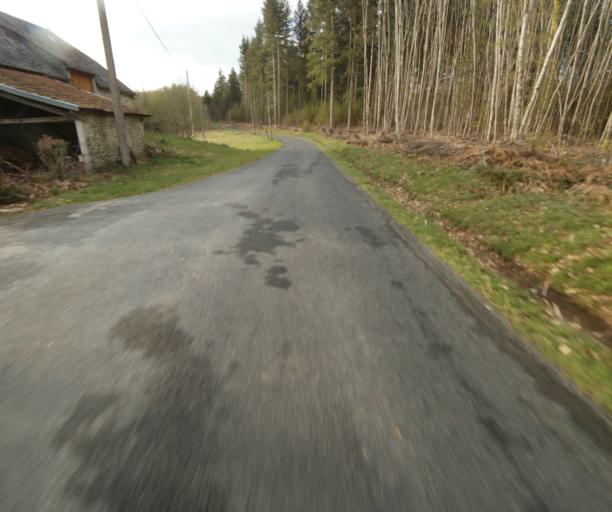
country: FR
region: Limousin
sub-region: Departement de la Correze
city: Argentat
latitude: 45.2188
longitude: 1.9397
